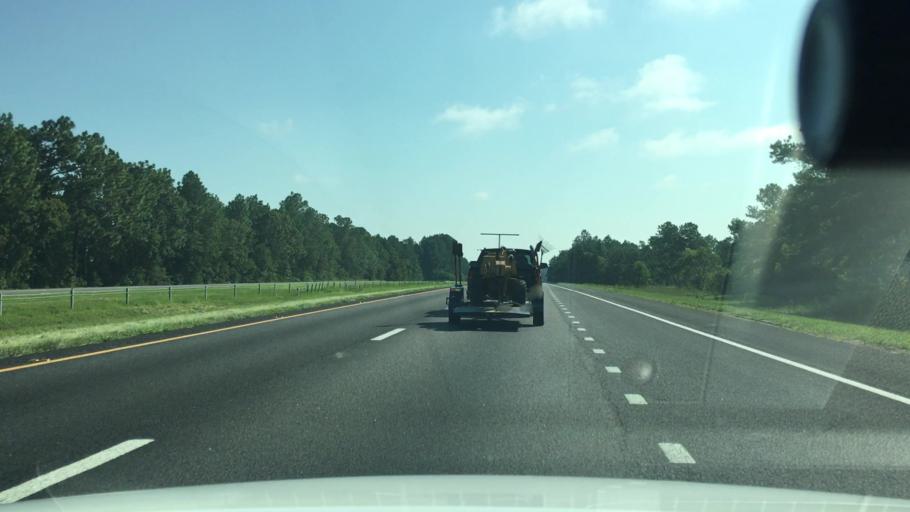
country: US
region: South Carolina
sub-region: Aiken County
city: Graniteville
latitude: 33.6095
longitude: -81.8388
